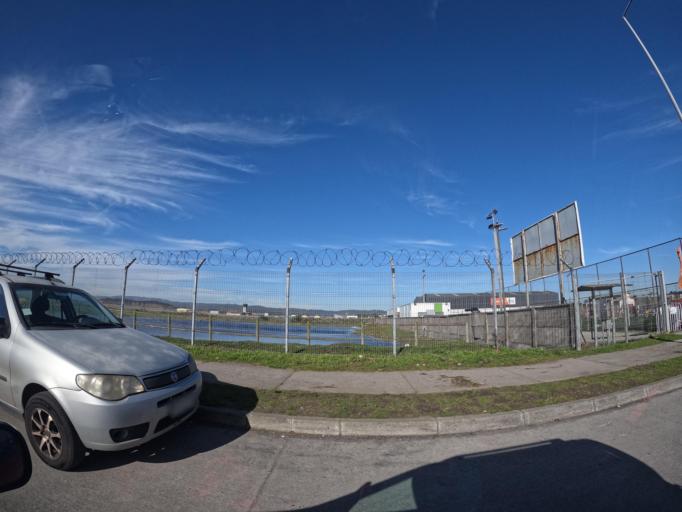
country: CL
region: Biobio
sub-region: Provincia de Concepcion
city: Concepcion
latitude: -36.7702
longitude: -73.0656
